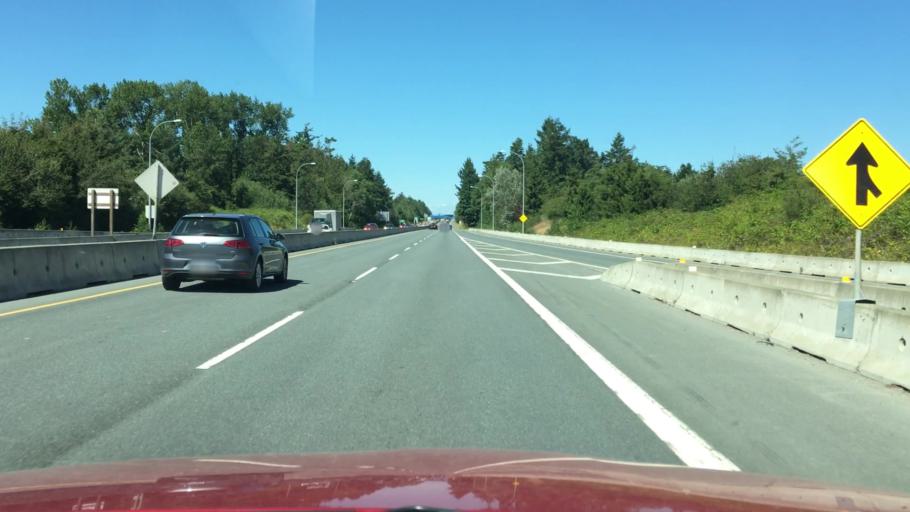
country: CA
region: British Columbia
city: North Saanich
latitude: 48.6319
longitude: -123.4114
